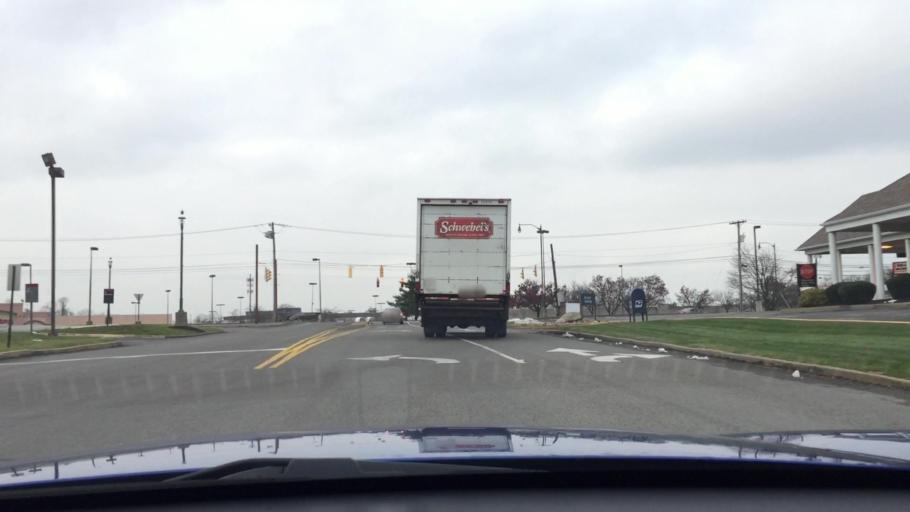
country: US
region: Pennsylvania
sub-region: Allegheny County
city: Pleasant Hills
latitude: 40.3434
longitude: -79.9406
